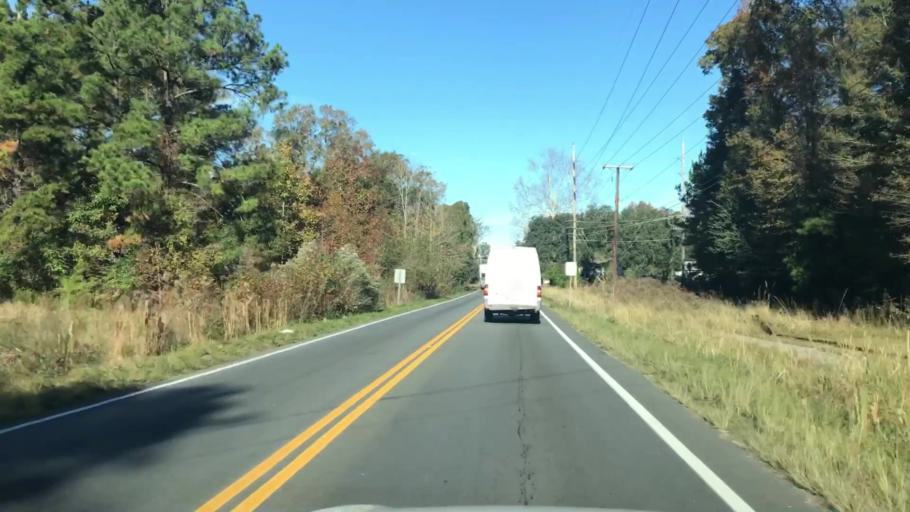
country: US
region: South Carolina
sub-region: Dorchester County
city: Summerville
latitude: 33.0033
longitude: -80.2332
